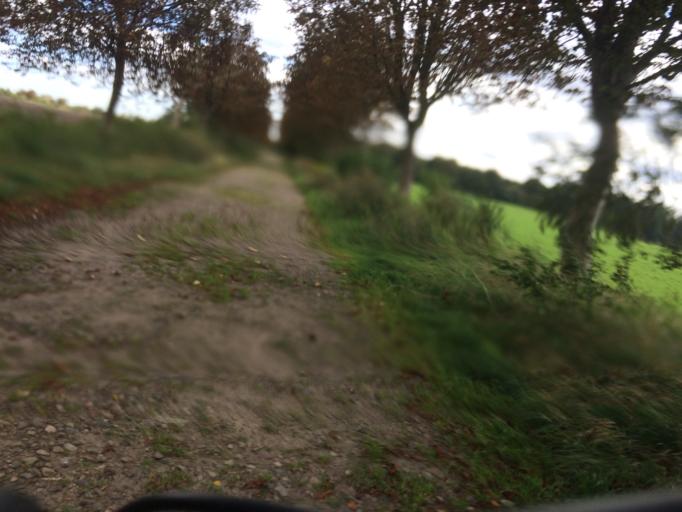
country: DE
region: Berlin
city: Blankenburg
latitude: 52.5821
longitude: 13.4560
